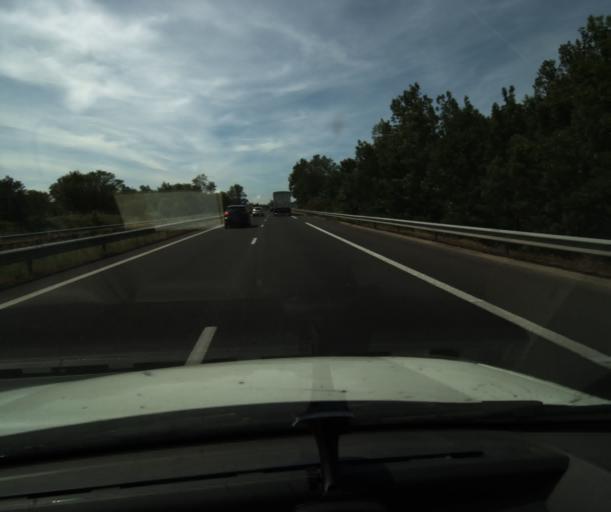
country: FR
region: Languedoc-Roussillon
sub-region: Departement de l'Aude
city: Villeneuve-la-Comptal
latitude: 43.2915
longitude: 1.9373
